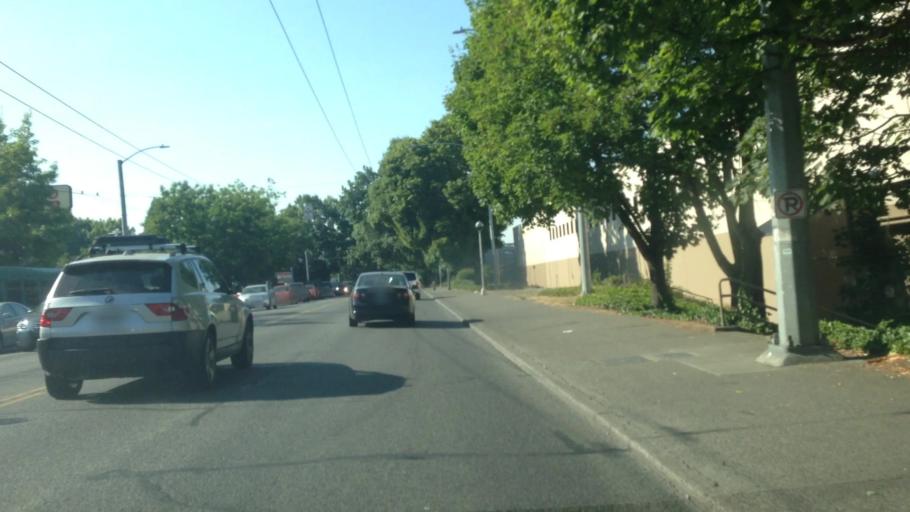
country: US
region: Washington
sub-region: King County
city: Seattle
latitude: 47.5785
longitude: -122.2982
